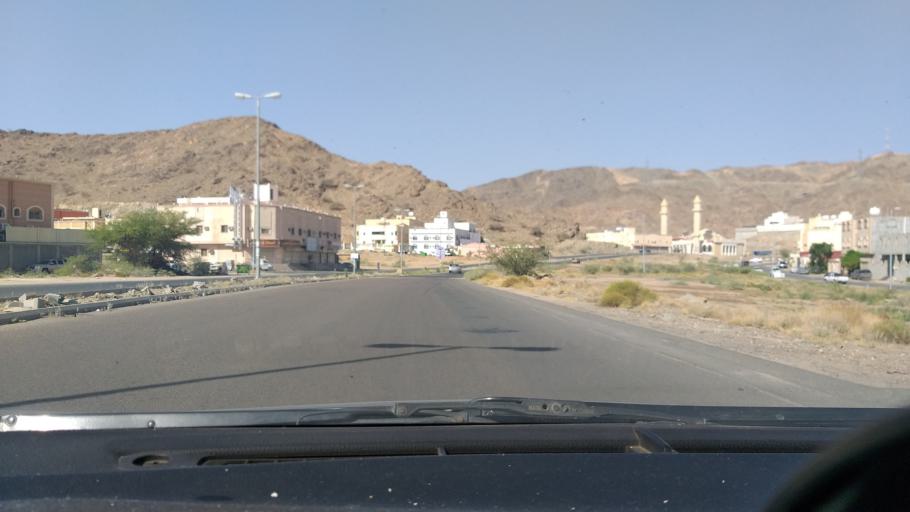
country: SA
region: Makkah
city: Ta'if
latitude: 21.2220
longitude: 40.3722
